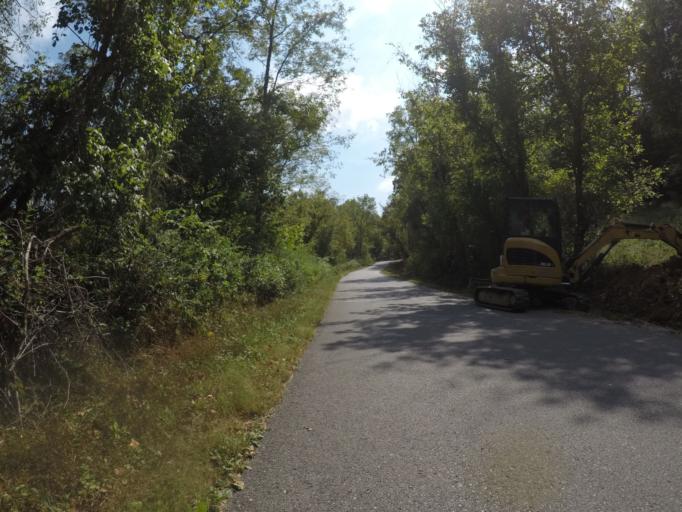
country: US
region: West Virginia
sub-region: Cabell County
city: Huntington
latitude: 38.4604
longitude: -82.4041
